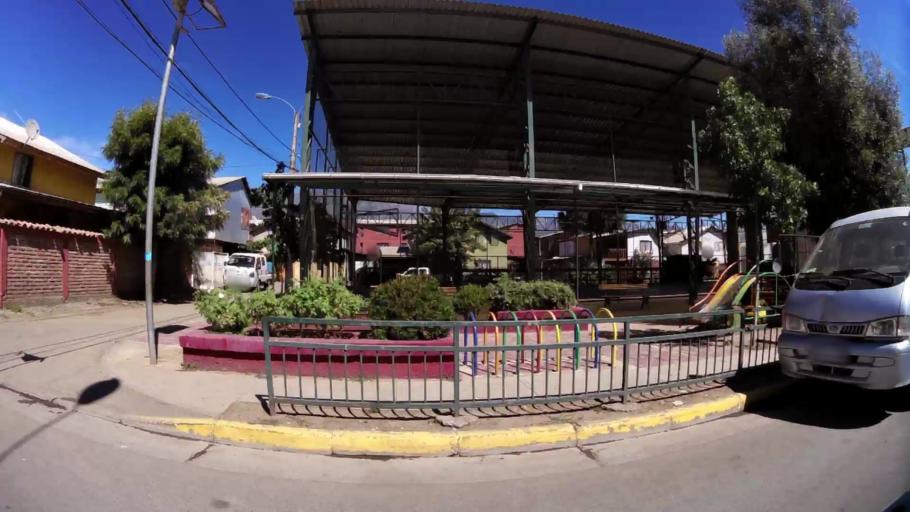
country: CL
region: O'Higgins
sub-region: Provincia de Cachapoal
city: Graneros
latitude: -33.9761
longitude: -70.7095
